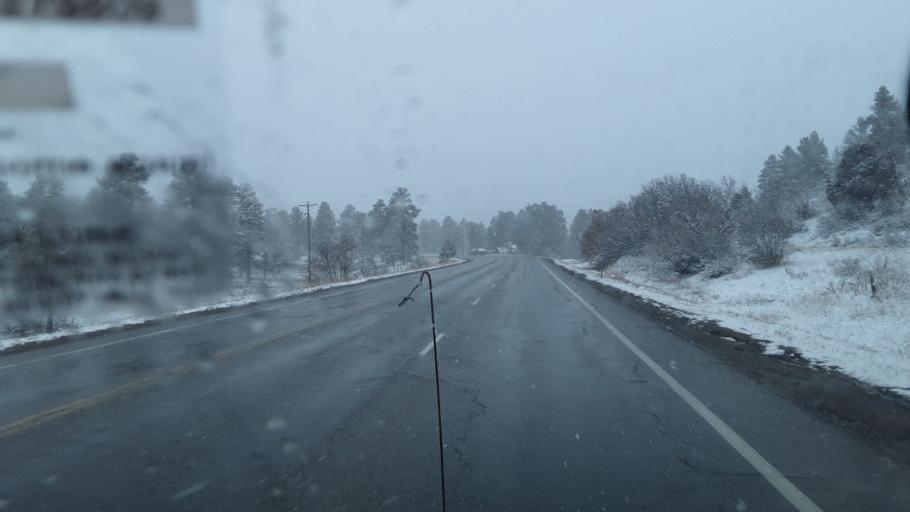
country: US
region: Colorado
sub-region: Archuleta County
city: Pagosa Springs
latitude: 37.2715
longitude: -107.0322
